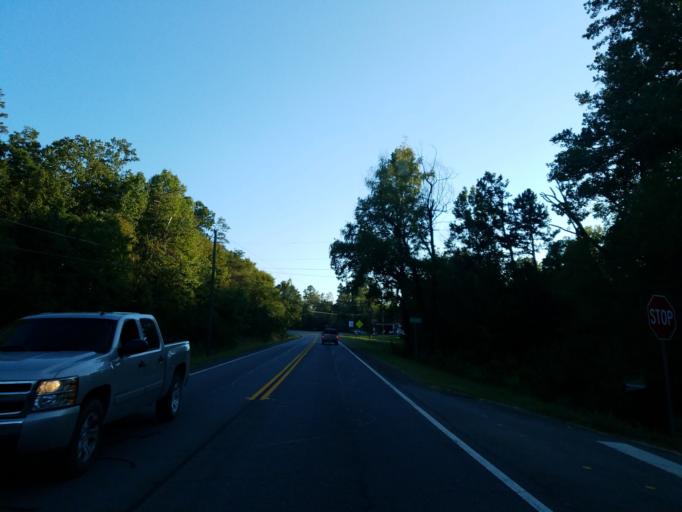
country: US
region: Georgia
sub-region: Bartow County
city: Rydal
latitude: 34.3513
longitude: -84.7231
